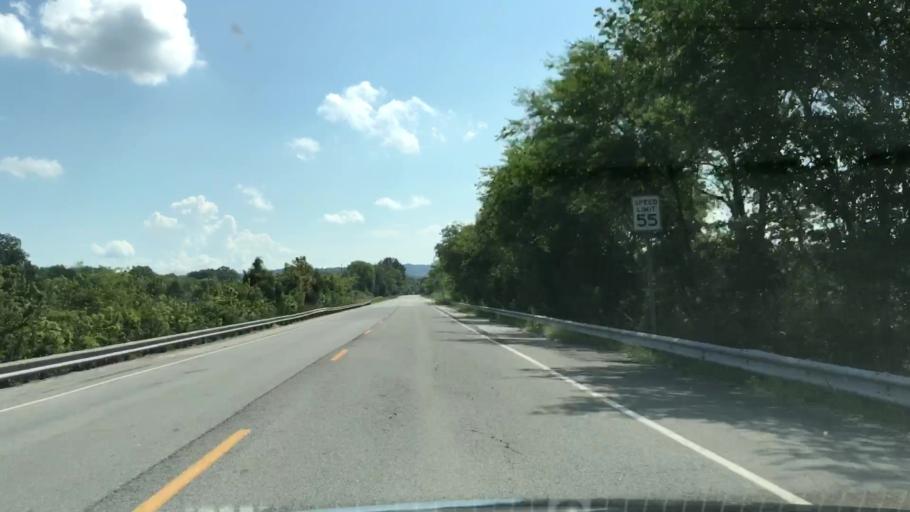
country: US
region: Tennessee
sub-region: Trousdale County
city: Hartsville
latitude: 36.3632
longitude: -86.0659
